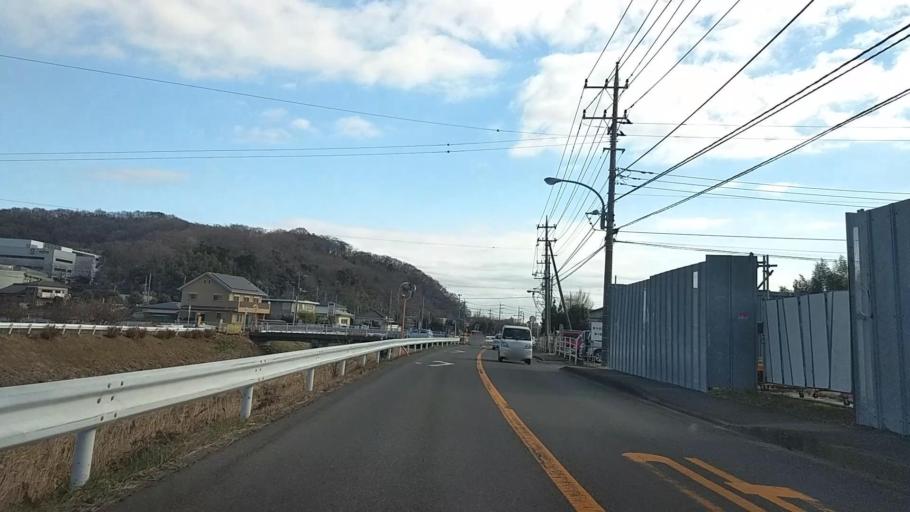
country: JP
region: Kanagawa
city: Isehara
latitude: 35.4354
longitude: 139.3111
